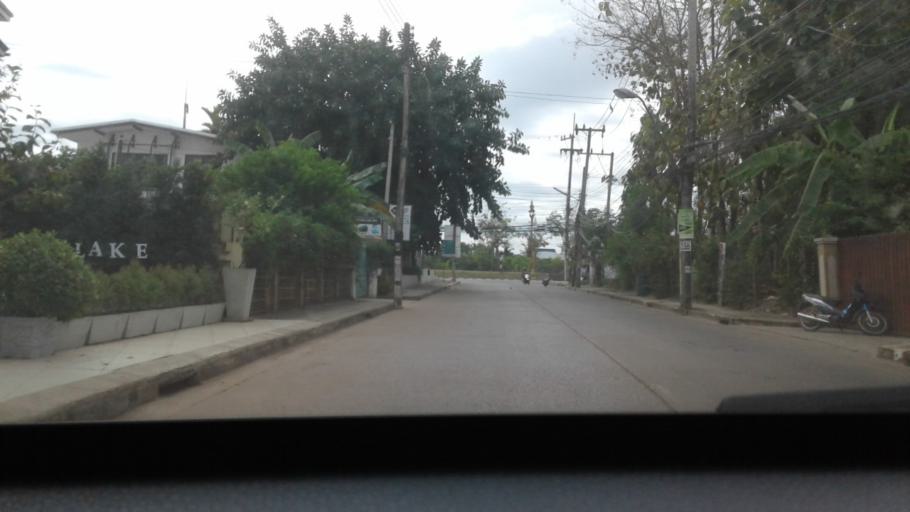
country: TH
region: Changwat Udon Thani
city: Udon Thani
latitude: 17.4224
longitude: 102.7827
